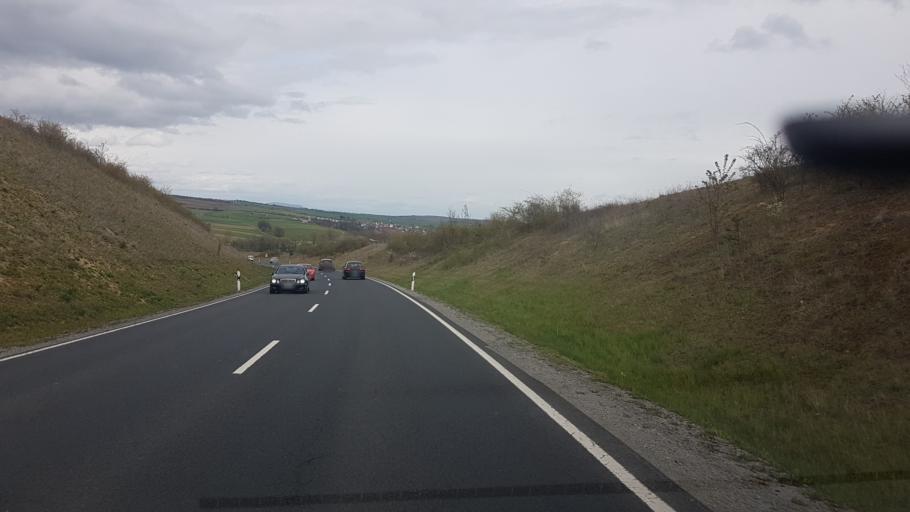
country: DE
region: Bavaria
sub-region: Regierungsbezirk Unterfranken
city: Hollstadt
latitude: 50.3299
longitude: 10.3079
